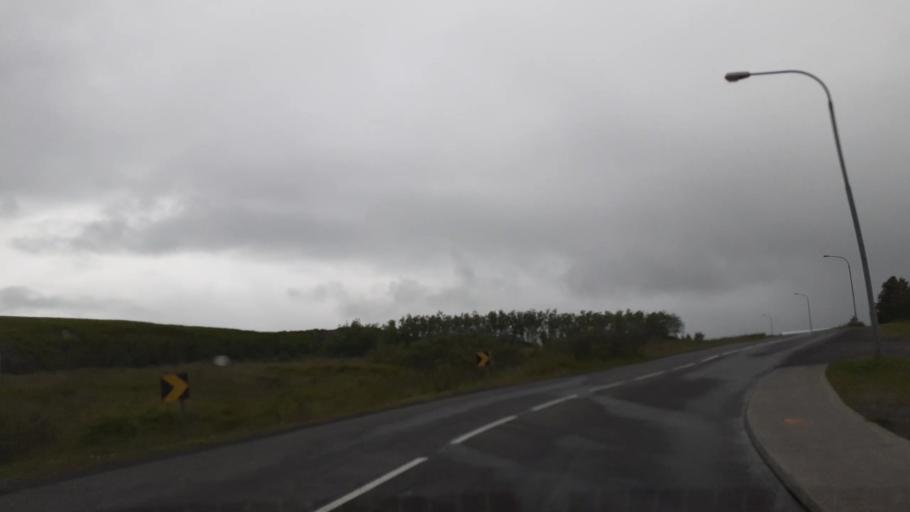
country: IS
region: East
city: Egilsstadir
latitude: 65.7517
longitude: -14.8343
